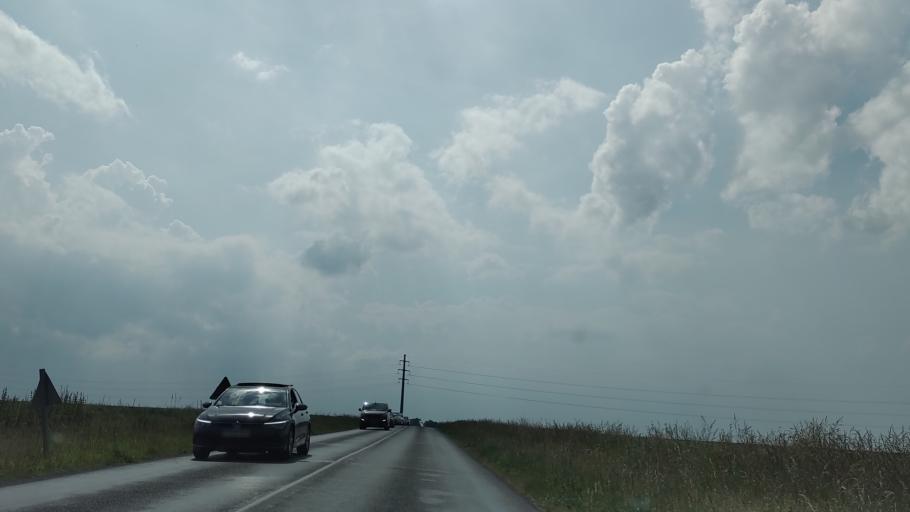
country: FR
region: Ile-de-France
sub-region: Departement de Seine-et-Marne
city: Juilly
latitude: 49.0101
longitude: 2.6968
